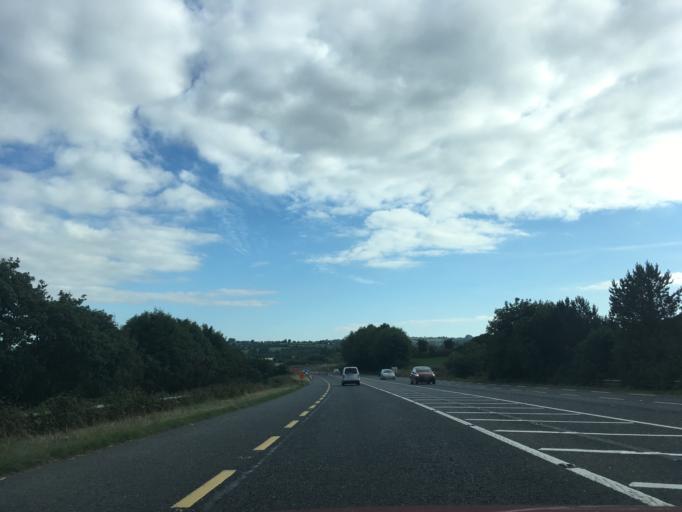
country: IE
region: Leinster
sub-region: Loch Garman
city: New Ross
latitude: 52.3646
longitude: -7.0125
